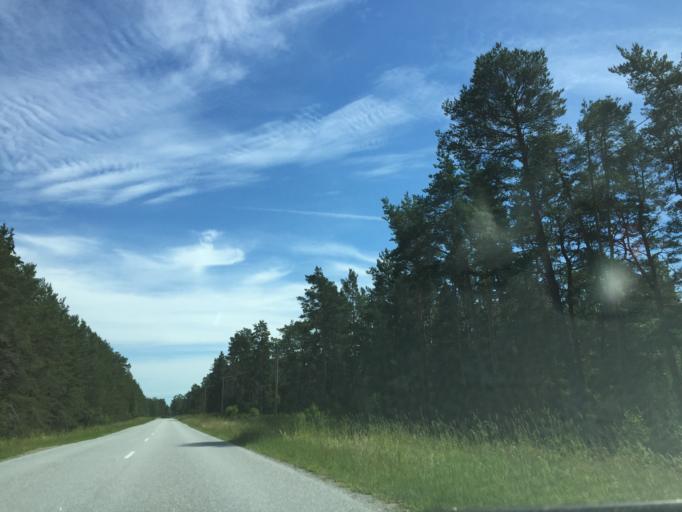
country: LV
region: Rojas
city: Roja
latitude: 57.5812
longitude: 22.6220
